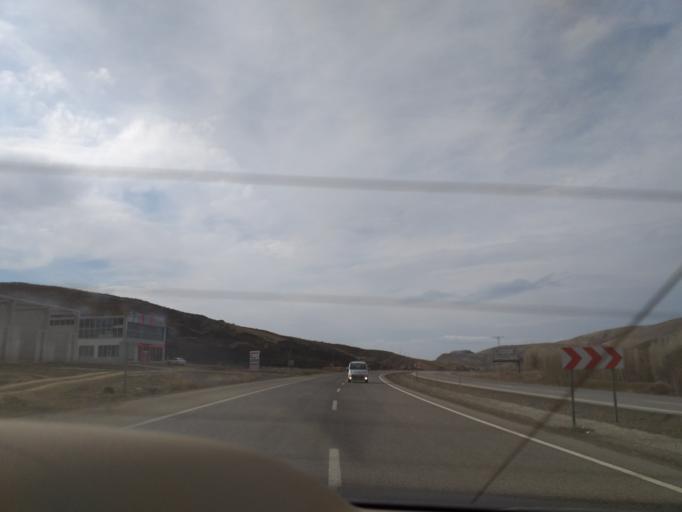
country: TR
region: Yozgat
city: Yozgat
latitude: 39.7865
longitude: 34.7567
